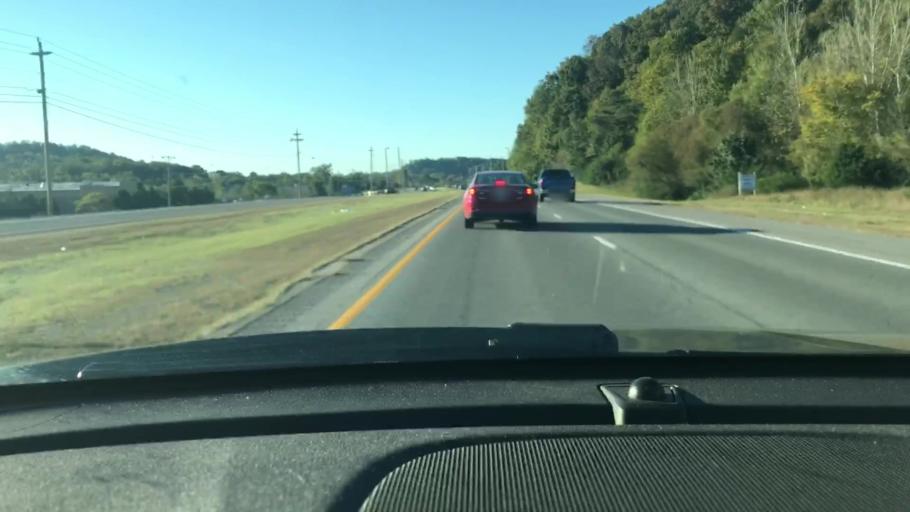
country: US
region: Tennessee
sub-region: Cheatham County
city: Ashland City
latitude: 36.2475
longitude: -87.0294
